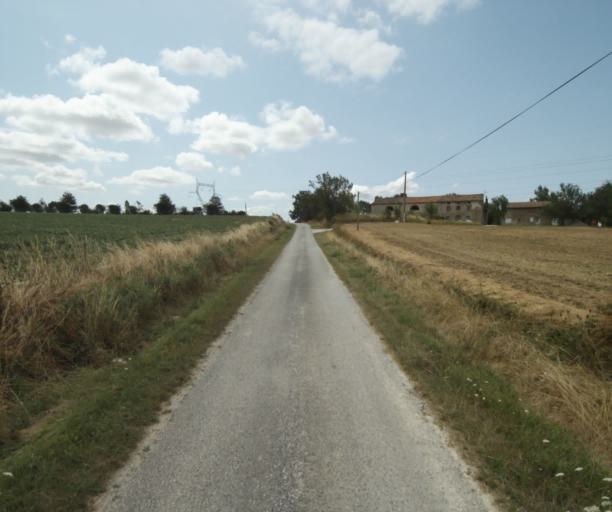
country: FR
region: Midi-Pyrenees
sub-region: Departement de la Haute-Garonne
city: Saint-Felix-Lauragais
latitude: 43.4171
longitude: 1.9064
